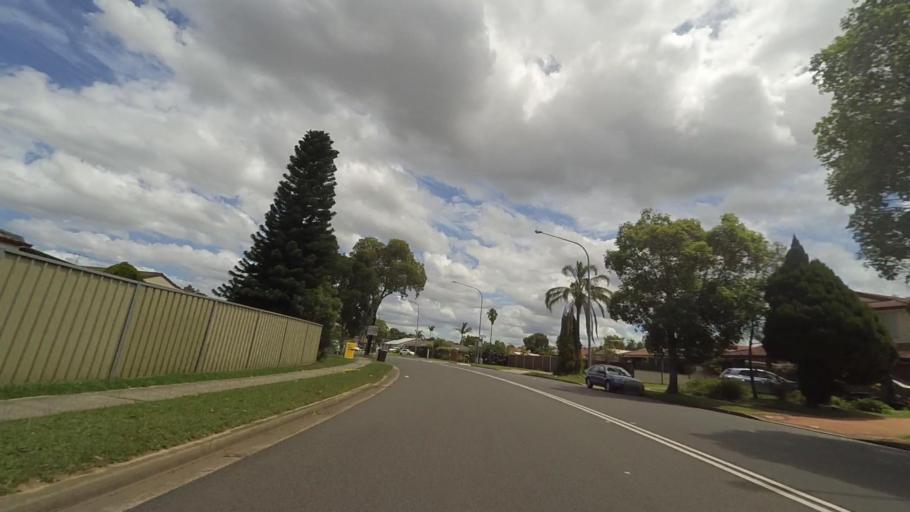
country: AU
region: New South Wales
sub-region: Fairfield
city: Fairfield Heights
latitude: -33.8681
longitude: 150.9116
